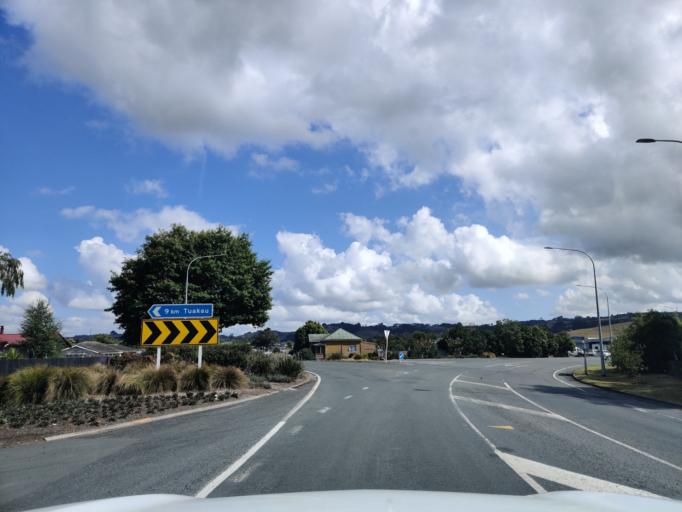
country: NZ
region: Auckland
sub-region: Auckland
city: Pukekohe East
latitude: -37.2449
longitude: 175.0204
